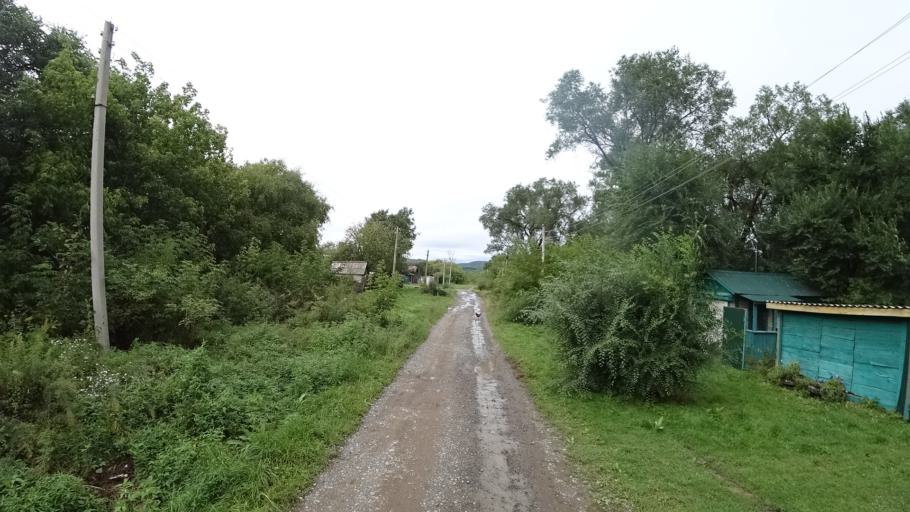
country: RU
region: Primorskiy
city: Lyalichi
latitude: 44.0796
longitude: 132.4810
